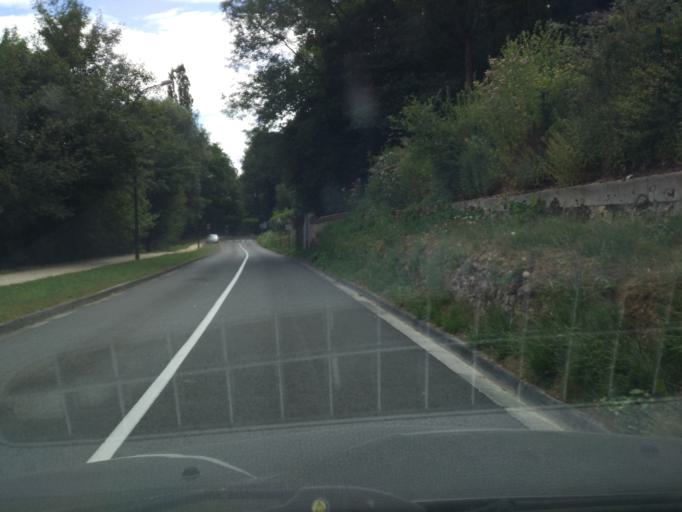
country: FR
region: Ile-de-France
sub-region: Departement de l'Essonne
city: Villiers-le-Bacle
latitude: 48.7219
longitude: 2.1223
